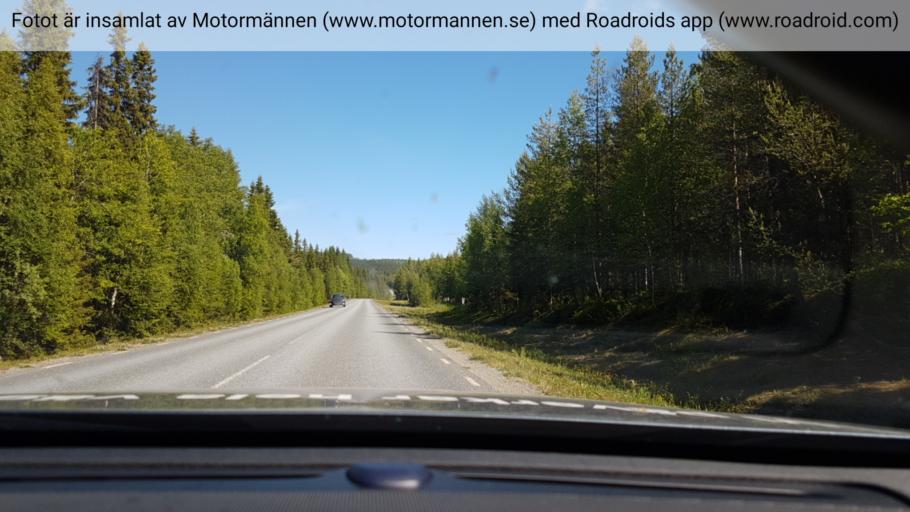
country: SE
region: Vaesterbotten
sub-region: Vilhelmina Kommun
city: Vilhelmina
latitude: 64.6502
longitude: 16.9854
